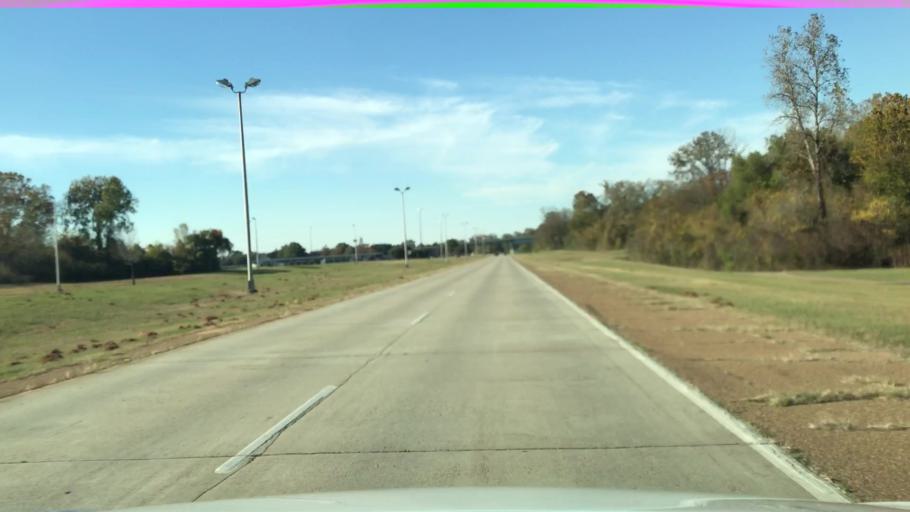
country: US
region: Louisiana
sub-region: Bossier Parish
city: Bossier City
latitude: 32.4862
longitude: -93.6956
